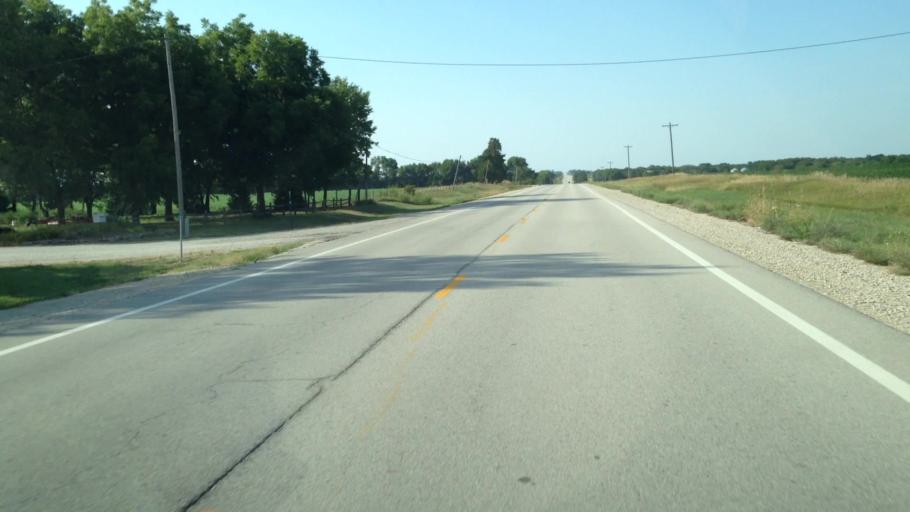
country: US
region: Kansas
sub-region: Anderson County
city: Garnett
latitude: 38.0990
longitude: -95.2430
